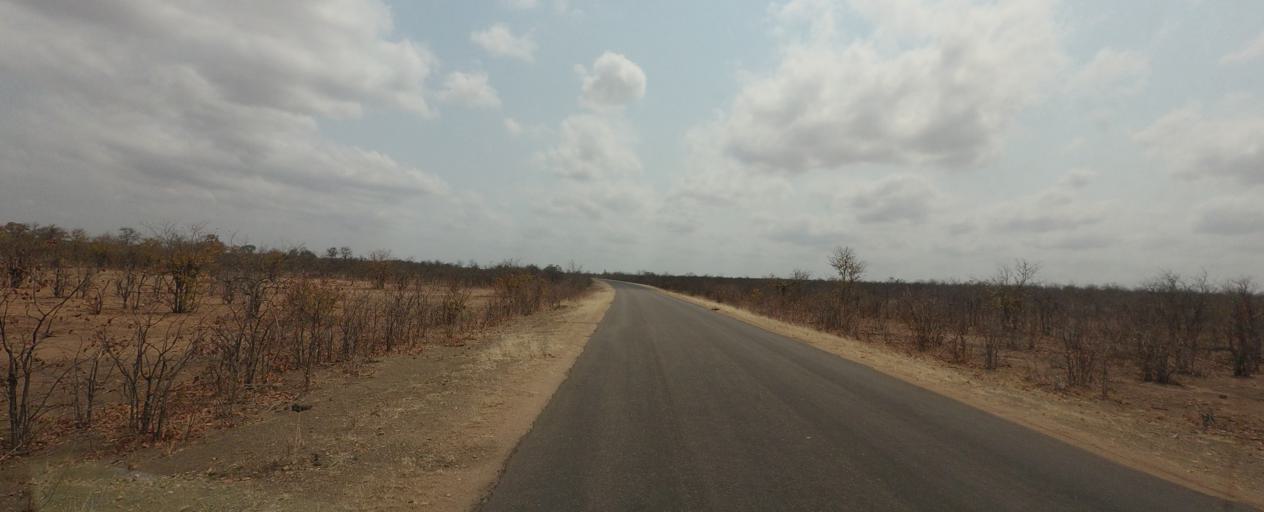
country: ZA
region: Limpopo
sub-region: Mopani District Municipality
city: Phalaborwa
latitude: -23.5984
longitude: 31.4551
